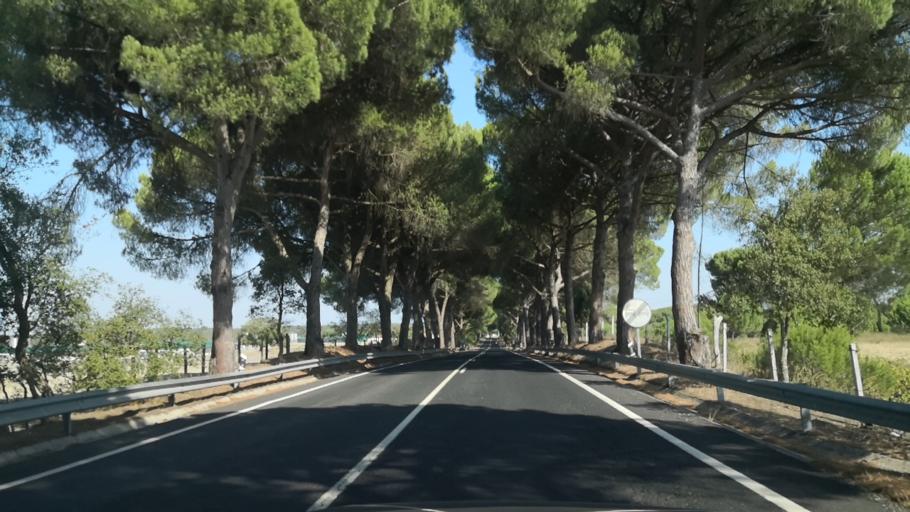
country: PT
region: Evora
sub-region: Vendas Novas
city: Vendas Novas
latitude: 38.7198
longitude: -8.6280
